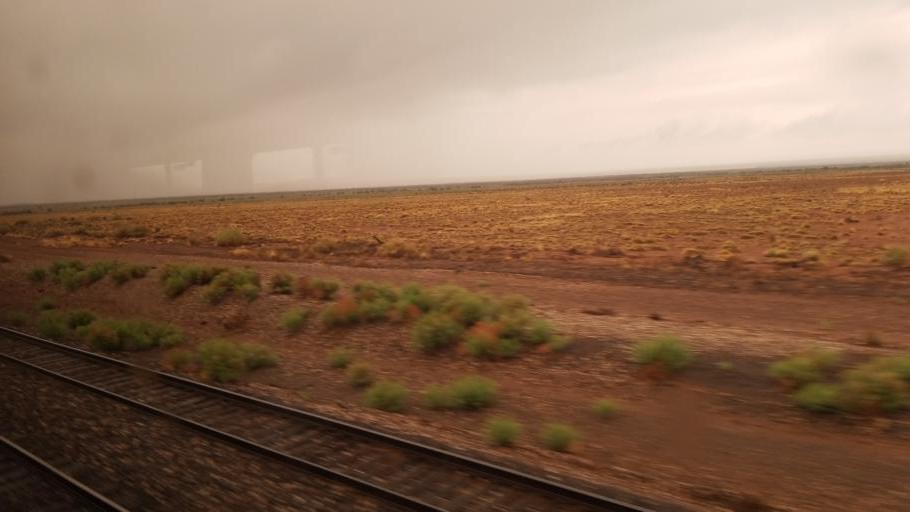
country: US
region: Arizona
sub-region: Navajo County
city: Joseph City
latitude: 34.9676
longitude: -110.5144
